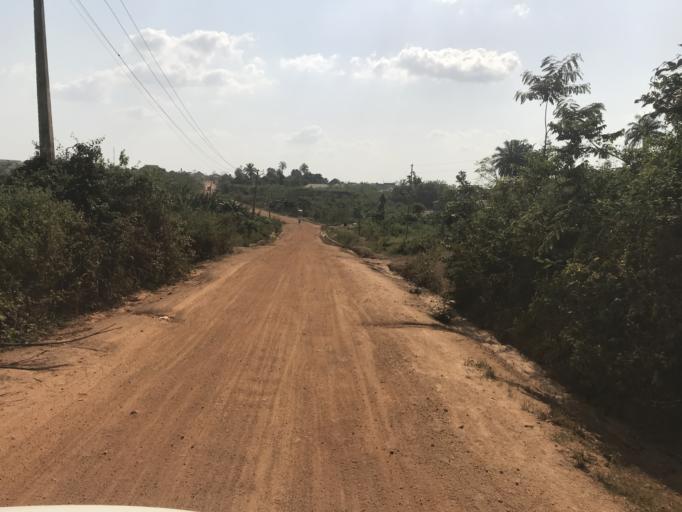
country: NG
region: Osun
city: Osogbo
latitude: 7.8209
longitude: 4.5649
